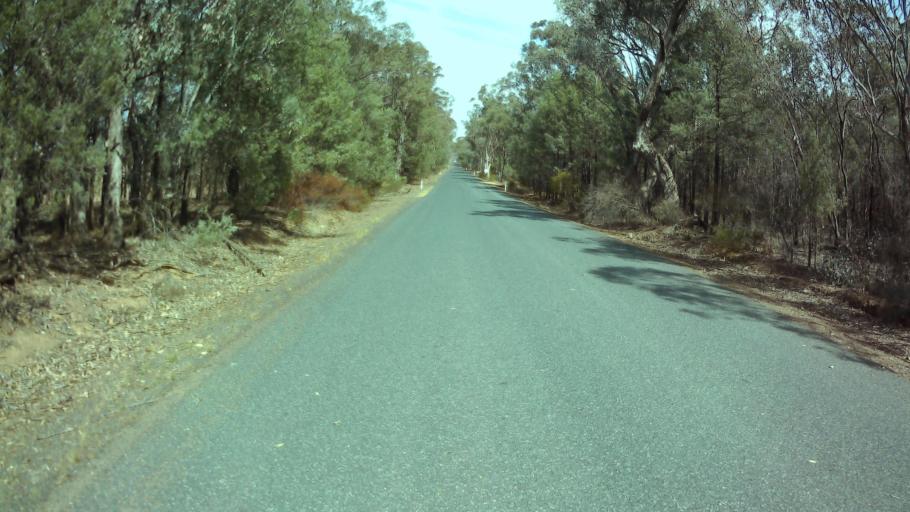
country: AU
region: New South Wales
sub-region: Weddin
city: Grenfell
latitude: -33.8064
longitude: 148.0467
